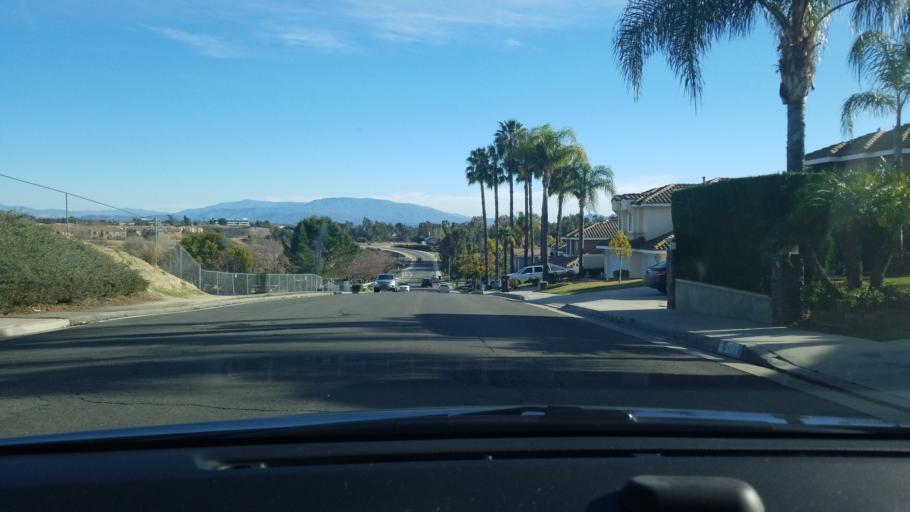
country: US
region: California
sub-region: Riverside County
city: Murrieta
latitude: 33.5685
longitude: -117.1950
